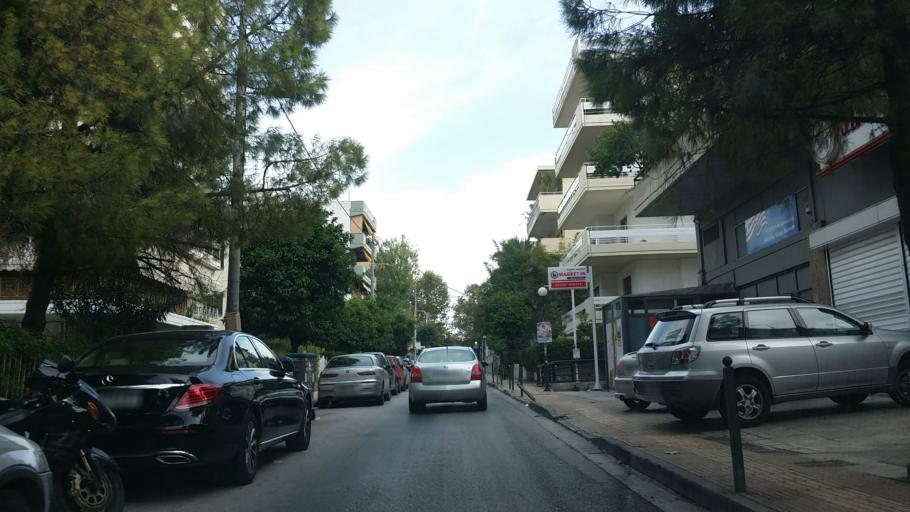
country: GR
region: Attica
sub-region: Nomarchia Athinas
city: Irakleio
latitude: 38.0473
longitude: 23.7680
